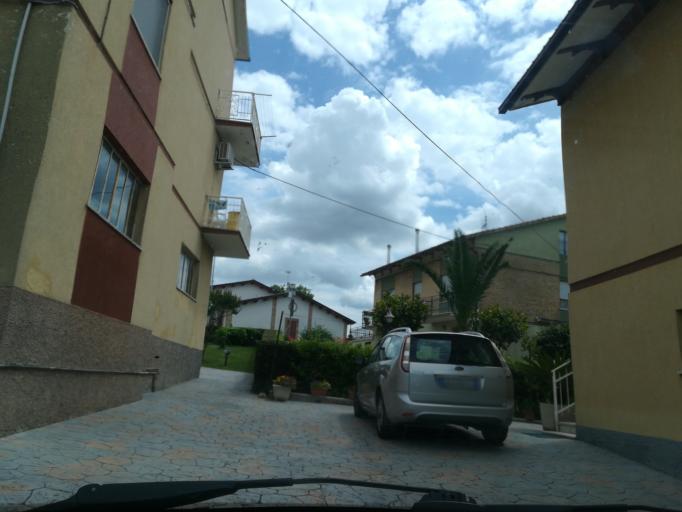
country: IT
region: The Marches
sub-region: Provincia di Macerata
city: Petriolo
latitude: 43.2253
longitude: 13.4779
